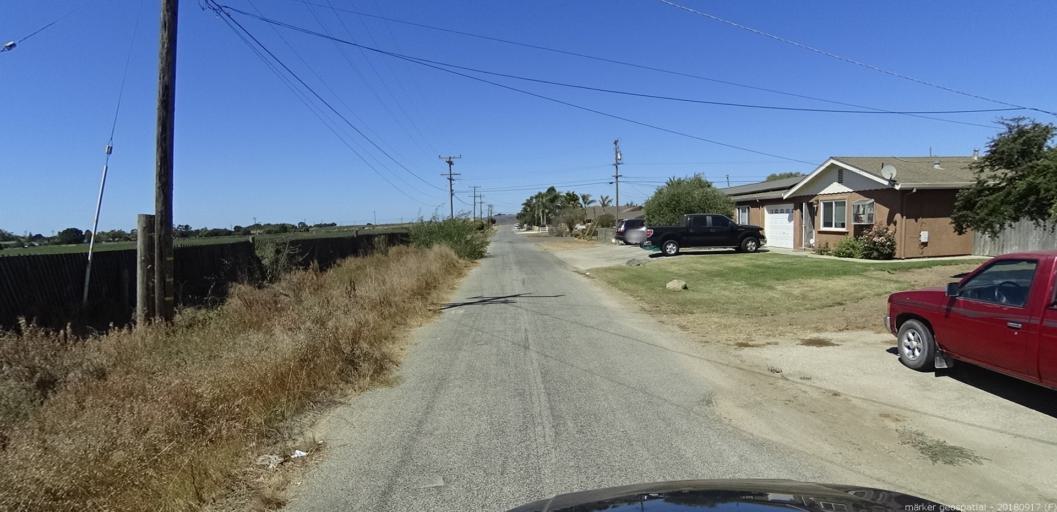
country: US
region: California
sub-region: Monterey County
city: Prunedale
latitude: 36.7492
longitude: -121.6207
